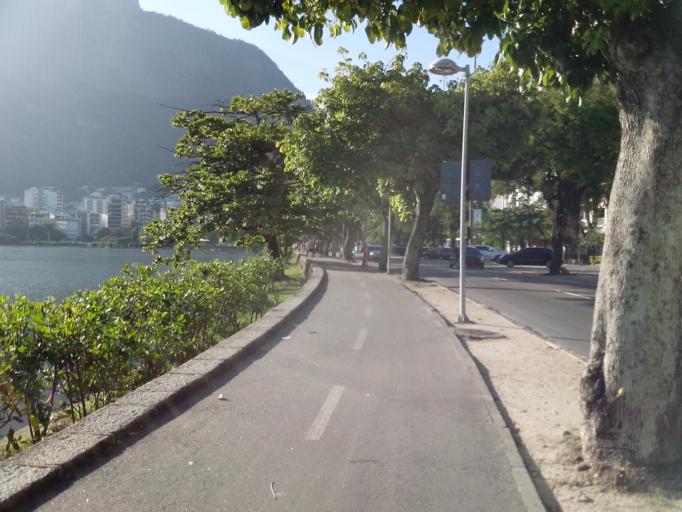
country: BR
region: Rio de Janeiro
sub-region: Rio De Janeiro
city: Rio de Janeiro
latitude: -22.9668
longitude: -43.2036
